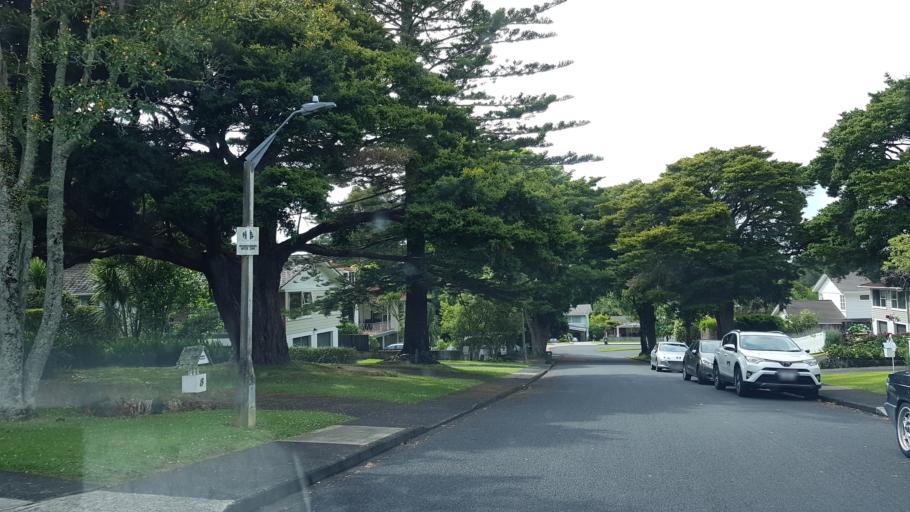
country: NZ
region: Auckland
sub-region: Auckland
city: North Shore
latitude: -36.7898
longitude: 174.7413
